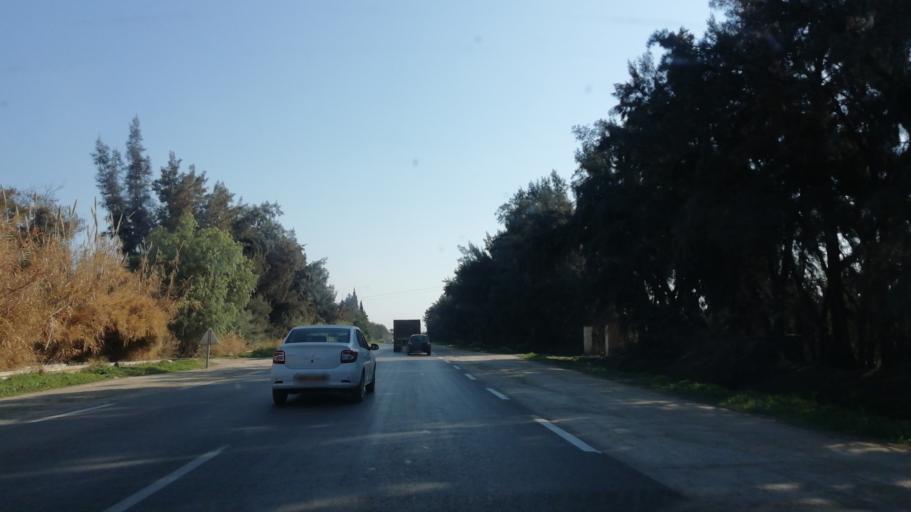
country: DZ
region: Relizane
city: Relizane
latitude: 35.7230
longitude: 0.4882
